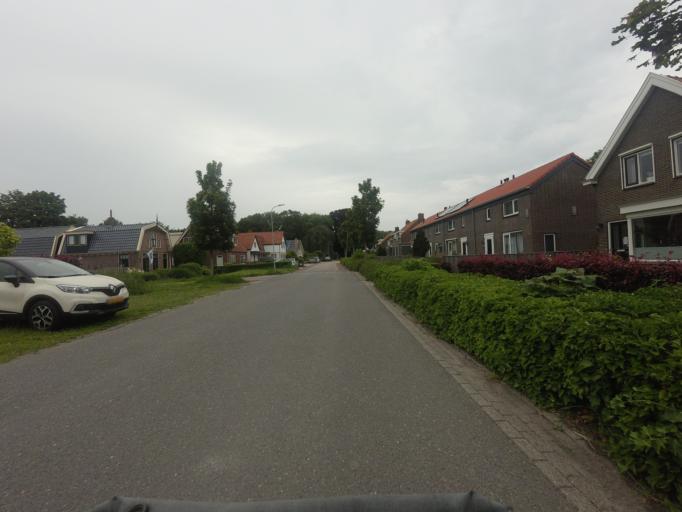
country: NL
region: North Holland
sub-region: Gemeente Hoorn
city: Hoorn
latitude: 52.6867
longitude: 5.1293
